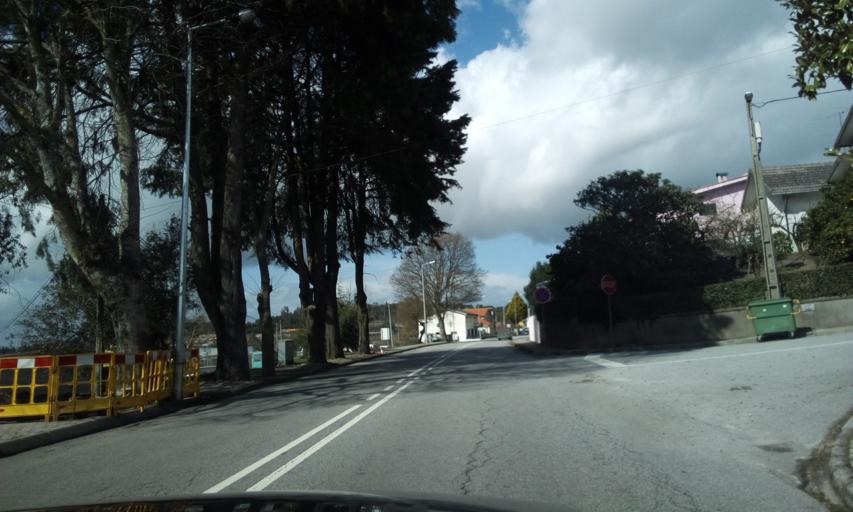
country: PT
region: Viseu
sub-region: Mangualde
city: Mangualde
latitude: 40.6138
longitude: -7.7597
